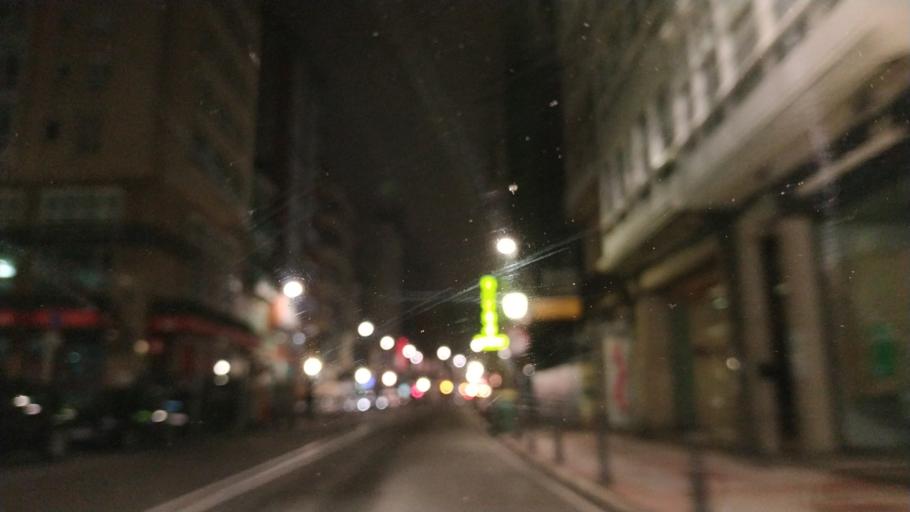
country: ES
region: Galicia
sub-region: Provincia da Coruna
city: A Coruna
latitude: 43.3686
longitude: -8.4049
